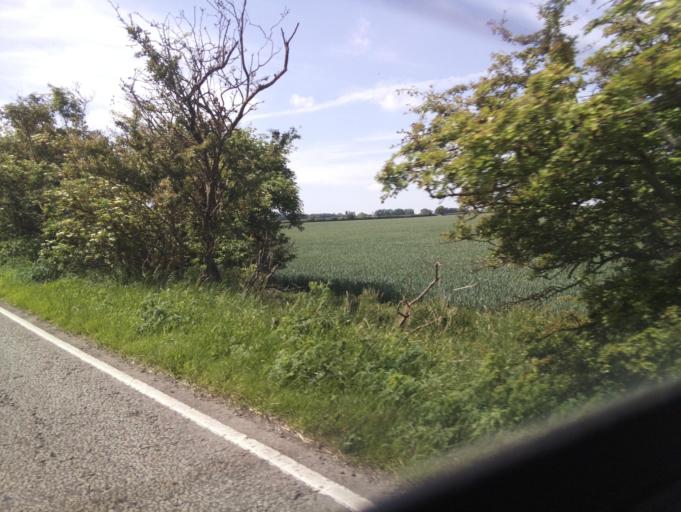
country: GB
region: England
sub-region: Lincolnshire
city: Dunholme
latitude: 53.3754
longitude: -0.5465
